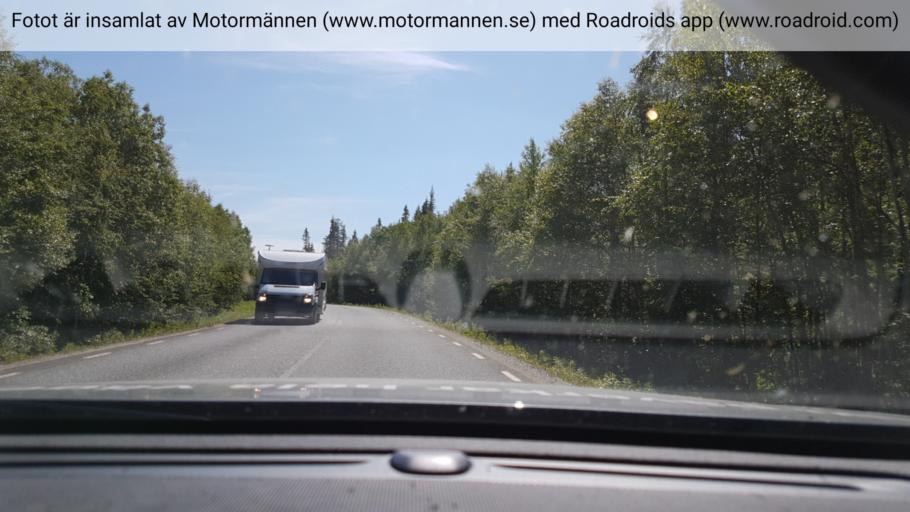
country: SE
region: Vaesterbotten
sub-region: Vilhelmina Kommun
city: Sjoberg
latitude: 64.7168
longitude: 15.3793
